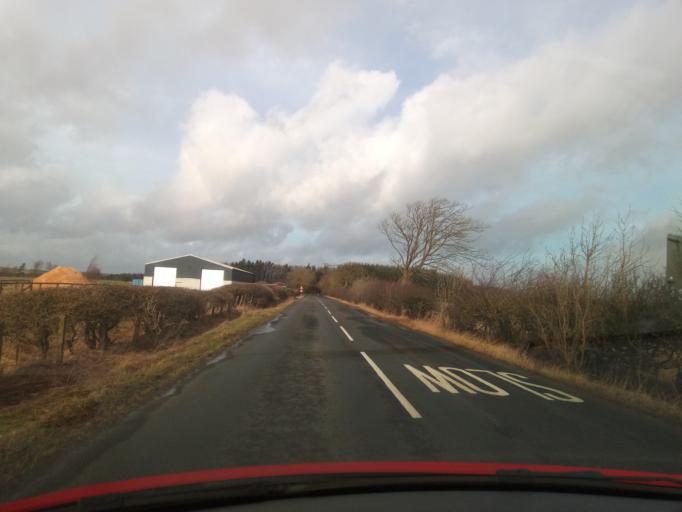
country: GB
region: England
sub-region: Northumberland
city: Rothley
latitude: 55.1071
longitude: -2.0089
